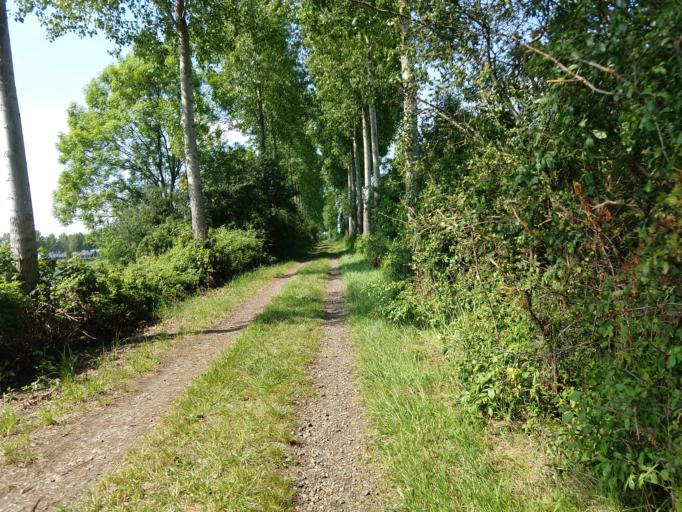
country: NL
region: Zeeland
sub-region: Gemeente Goes
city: Goes
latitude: 51.4300
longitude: 3.8355
